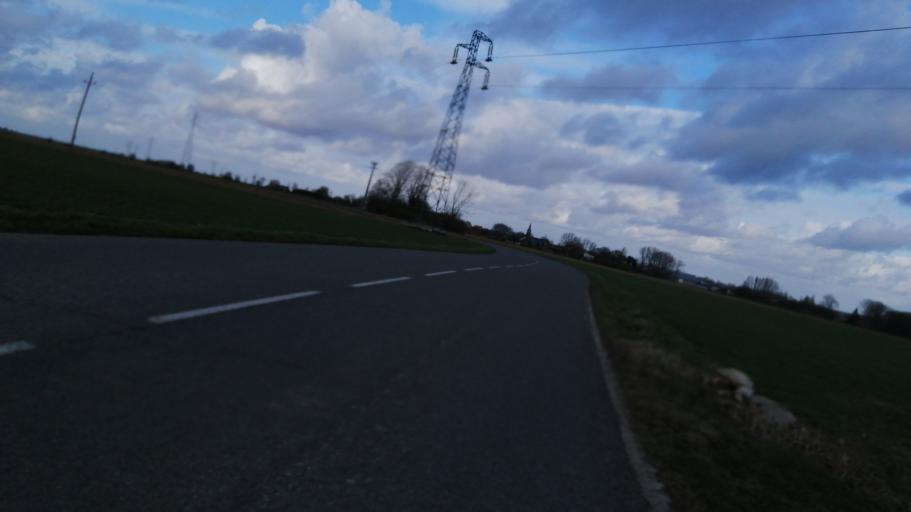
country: FR
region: Nord-Pas-de-Calais
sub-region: Departement du Pas-de-Calais
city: Beaurains
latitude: 50.2408
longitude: 2.8075
